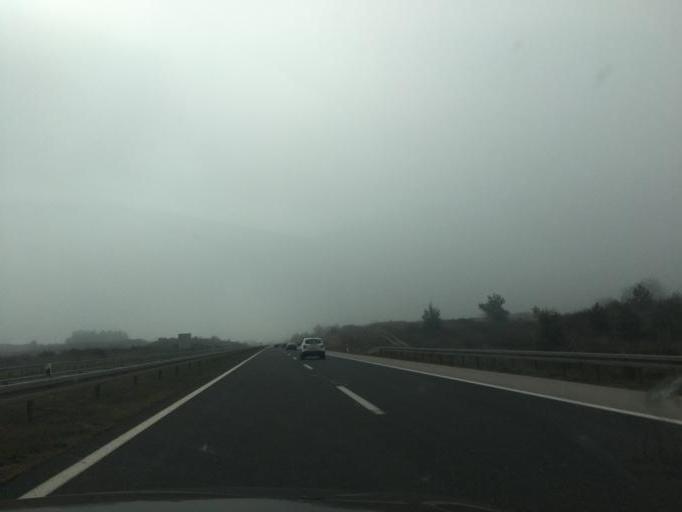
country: HR
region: Licko-Senjska
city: Gospic
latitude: 44.5523
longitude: 15.4320
